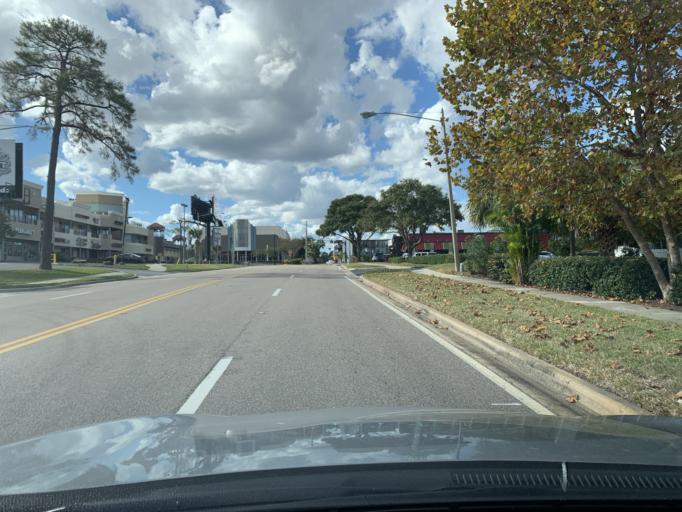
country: US
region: Florida
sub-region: Orange County
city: Tangelo Park
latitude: 28.4560
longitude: -81.4693
